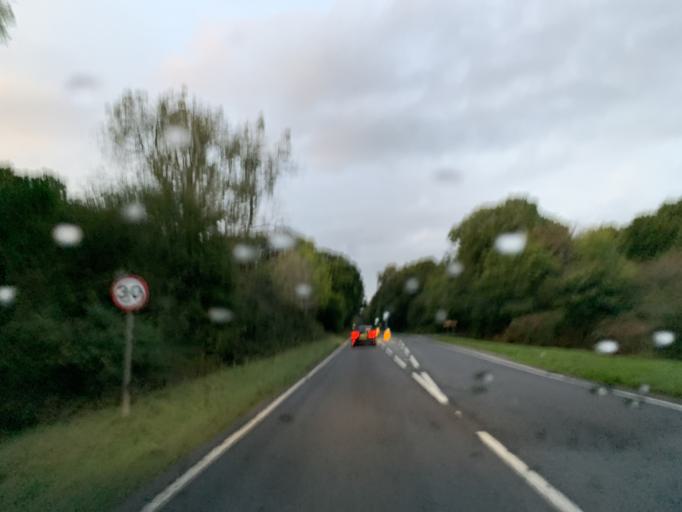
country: GB
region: England
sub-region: Hampshire
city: Brockenhurst
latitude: 50.8286
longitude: -1.5718
